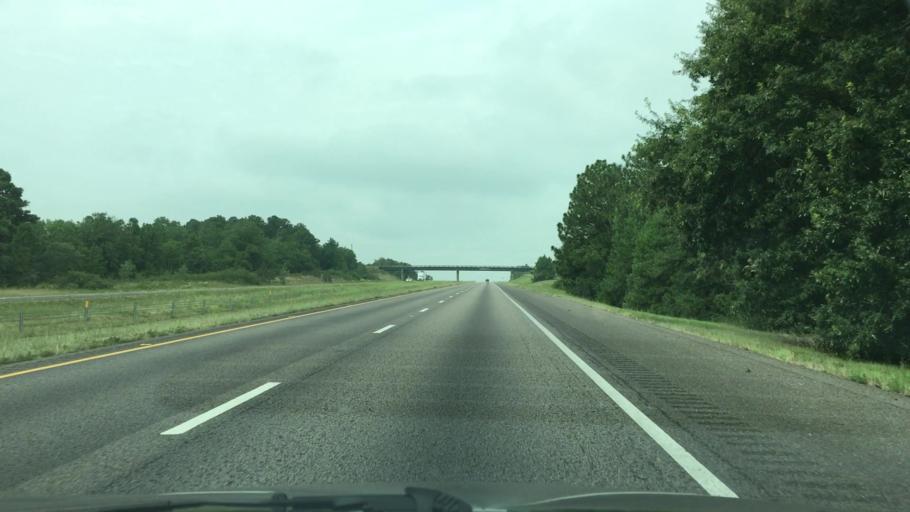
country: US
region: South Carolina
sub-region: Edgefield County
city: Murphys Estates
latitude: 33.5944
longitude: -81.8743
